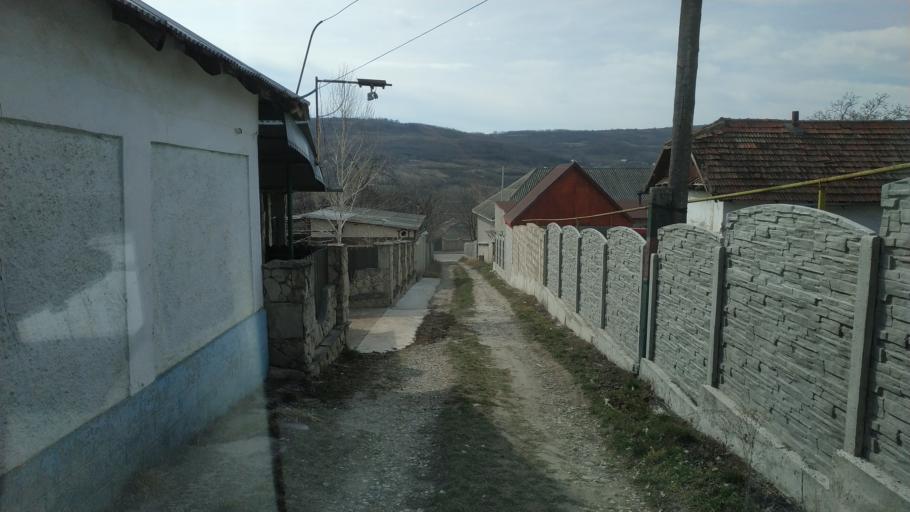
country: MD
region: Chisinau
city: Vatra
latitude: 47.0935
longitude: 28.6782
